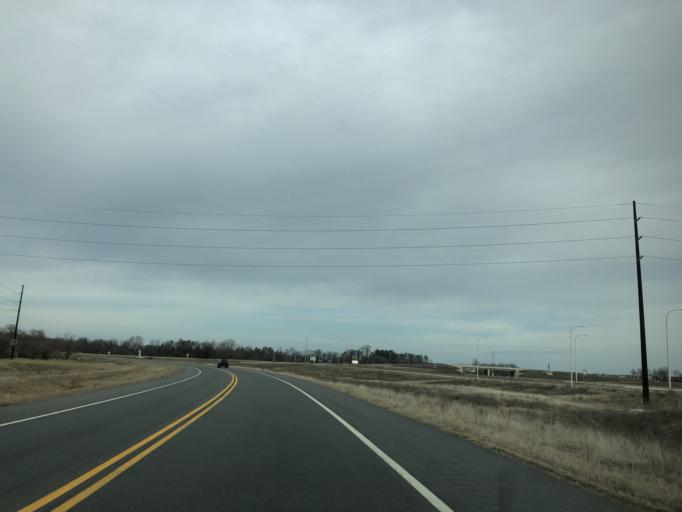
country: US
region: Delaware
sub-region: New Castle County
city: Middletown
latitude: 39.4416
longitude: -75.7559
